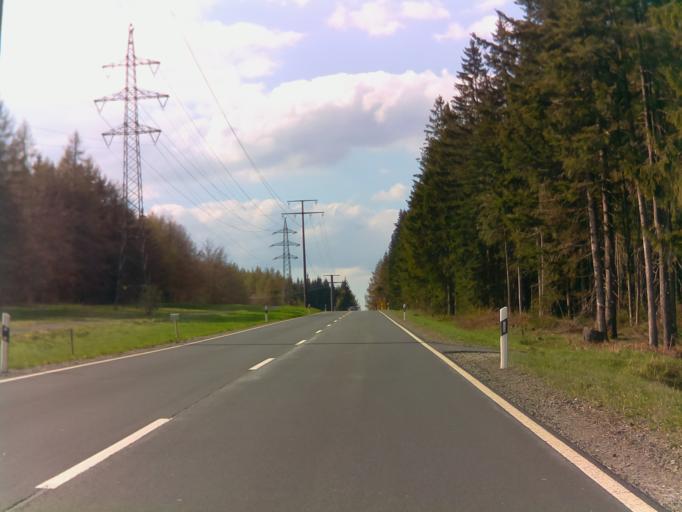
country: DE
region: Bavaria
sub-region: Upper Franconia
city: Tettau
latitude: 50.4754
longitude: 11.3073
